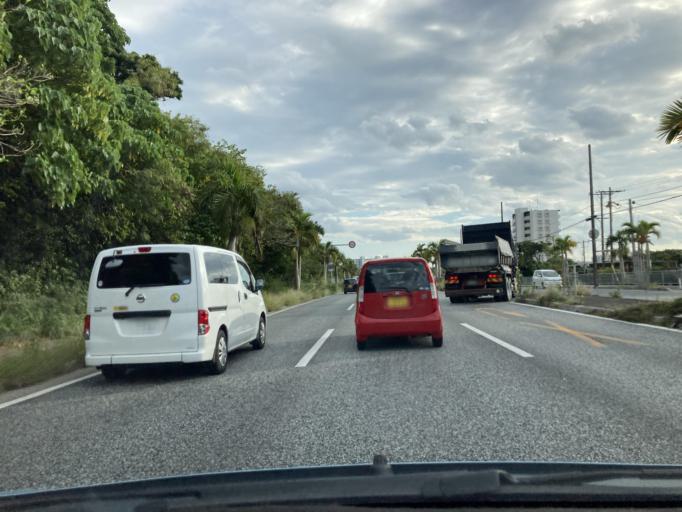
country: JP
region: Okinawa
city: Chatan
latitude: 26.3353
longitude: 127.7516
